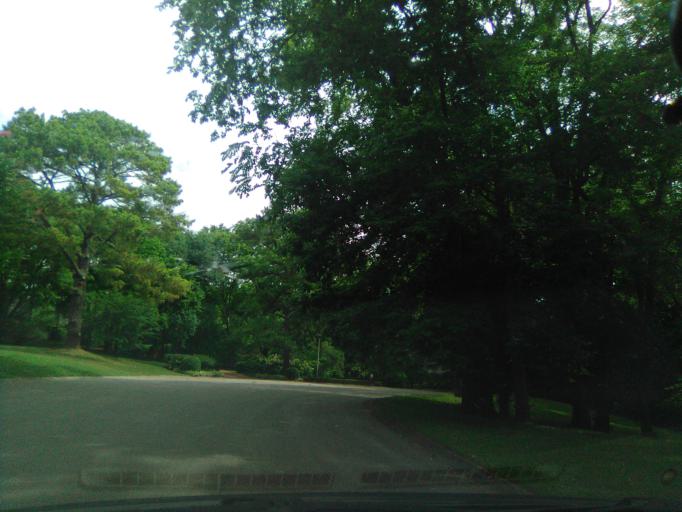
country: US
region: Tennessee
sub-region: Davidson County
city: Belle Meade
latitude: 36.1002
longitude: -86.8817
